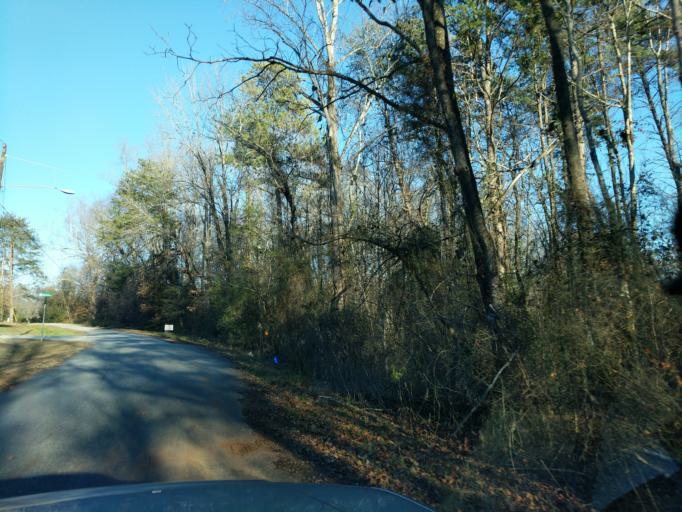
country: US
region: South Carolina
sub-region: Spartanburg County
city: Duncan
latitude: 34.9219
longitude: -82.1247
